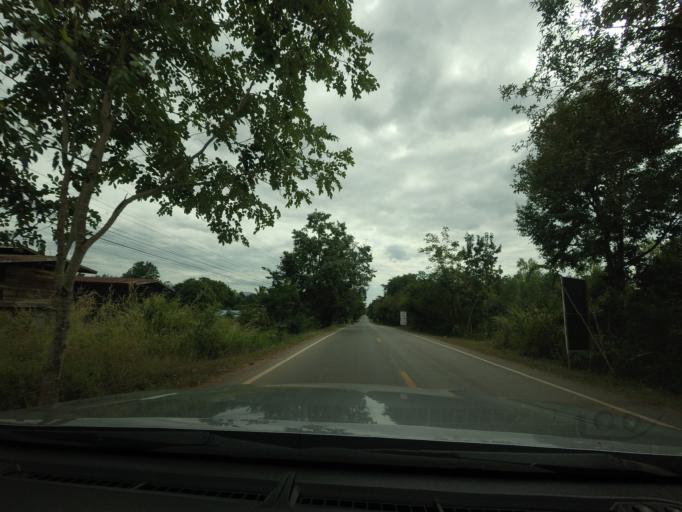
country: TH
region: Phitsanulok
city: Noen Maprang
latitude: 16.7008
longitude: 100.5904
